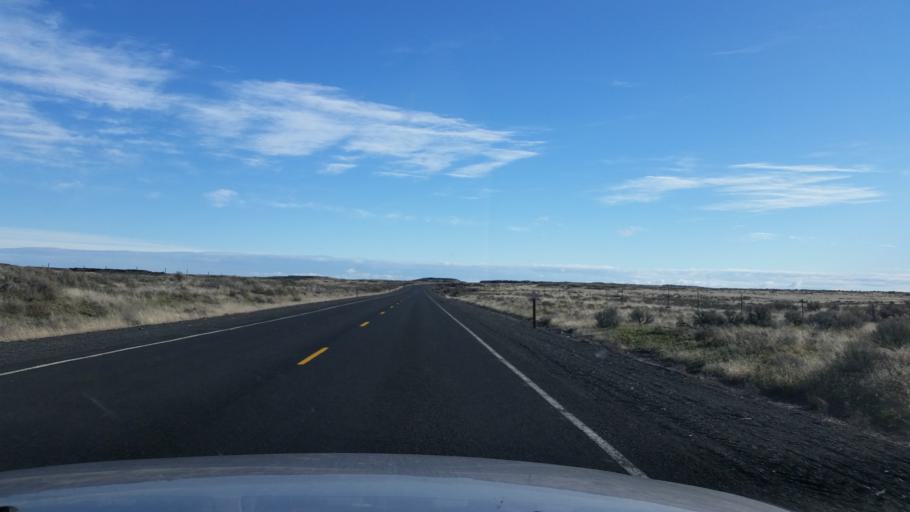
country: US
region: Washington
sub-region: Grant County
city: Warden
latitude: 47.3317
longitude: -118.8828
